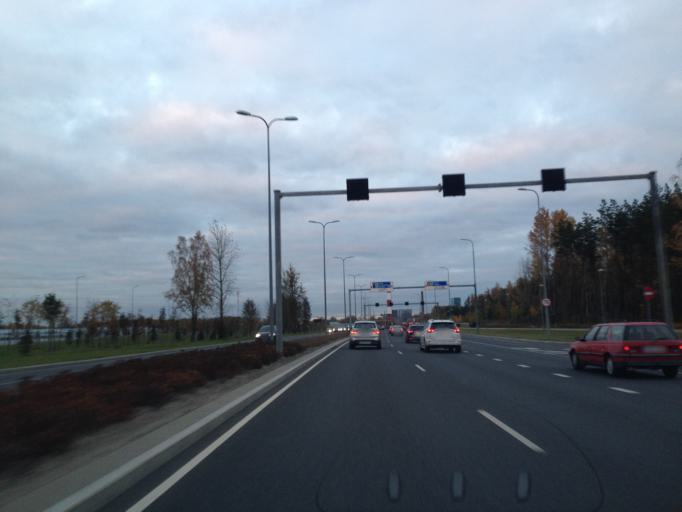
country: EE
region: Harju
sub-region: Tallinna linn
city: Tallinn
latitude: 59.4156
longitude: 24.7617
